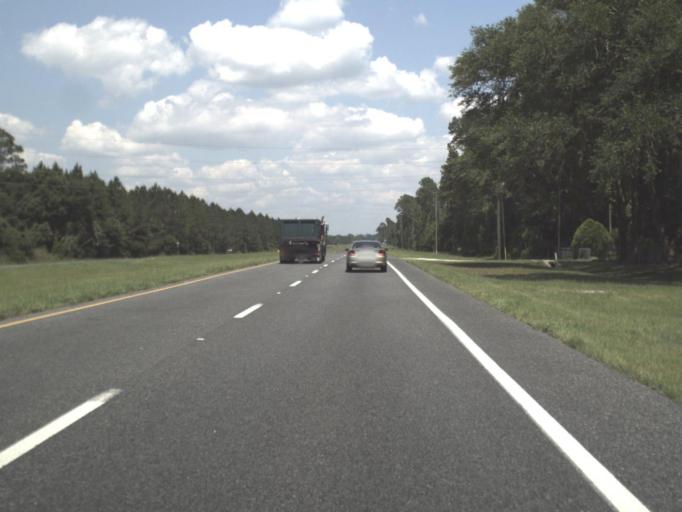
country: US
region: Florida
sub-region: Alachua County
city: Hawthorne
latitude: 29.5982
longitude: -82.1189
